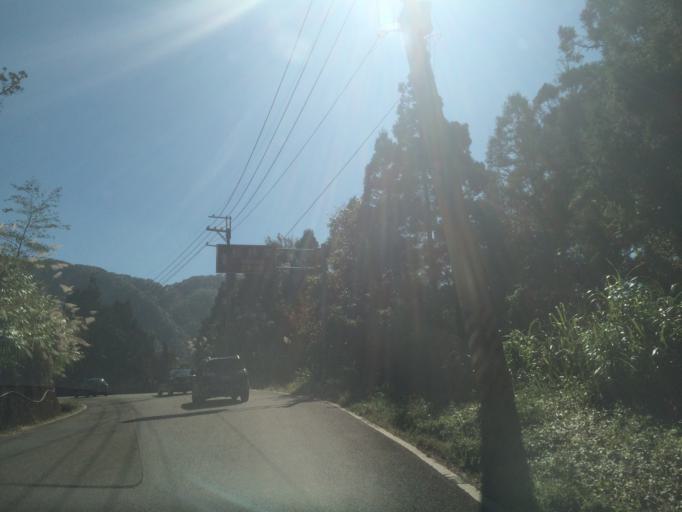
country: TW
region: Taiwan
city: Lugu
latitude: 23.6553
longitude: 120.7832
